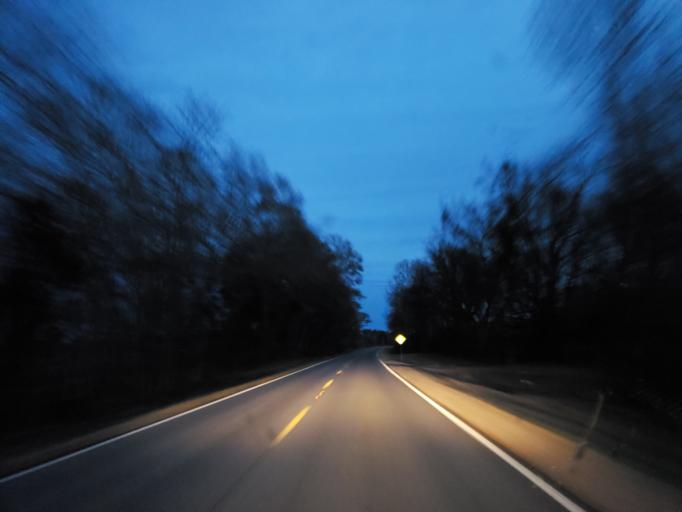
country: US
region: Alabama
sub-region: Greene County
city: Eutaw
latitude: 32.8880
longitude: -87.9443
